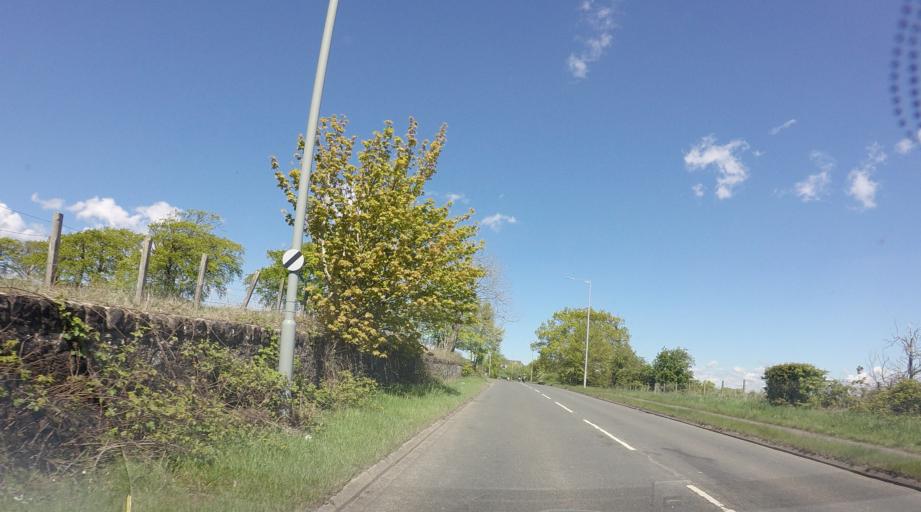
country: GB
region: Scotland
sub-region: Falkirk
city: Polmont
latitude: 55.9637
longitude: -3.6933
